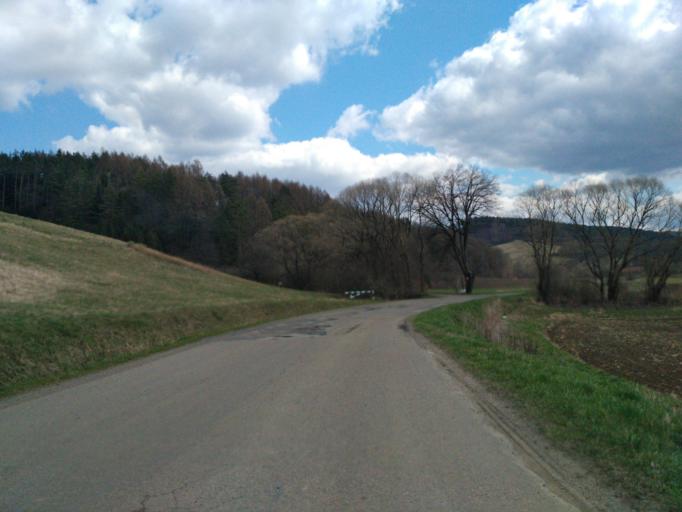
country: PL
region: Subcarpathian Voivodeship
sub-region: Powiat sanocki
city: Tyrawa Woloska
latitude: 49.6050
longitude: 22.3042
